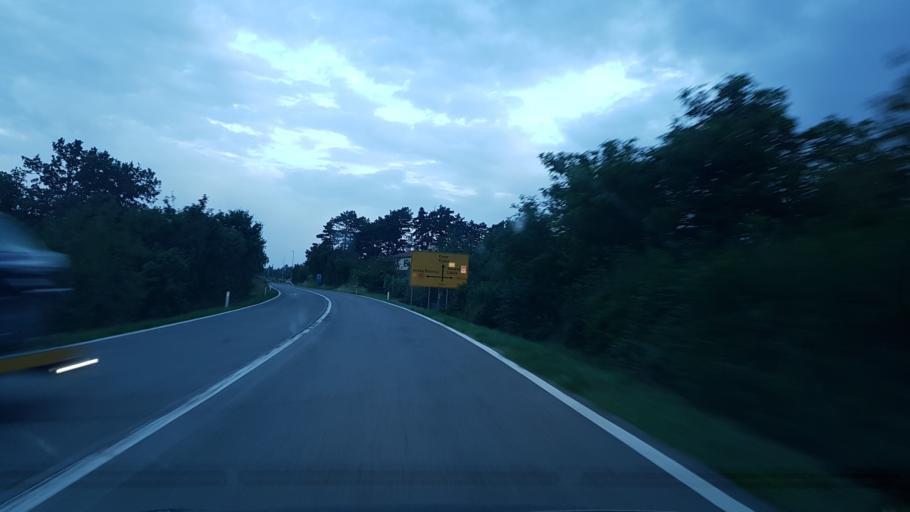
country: SI
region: Divaca
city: Divaca
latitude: 45.6826
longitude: 13.9720
